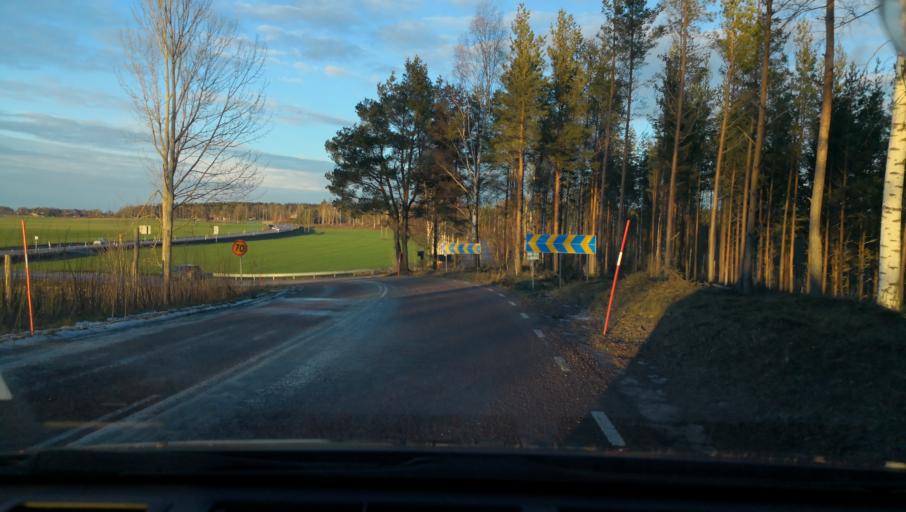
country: SE
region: Vaestmanland
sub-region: Vasteras
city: Tillberga
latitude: 59.7079
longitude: 16.5843
